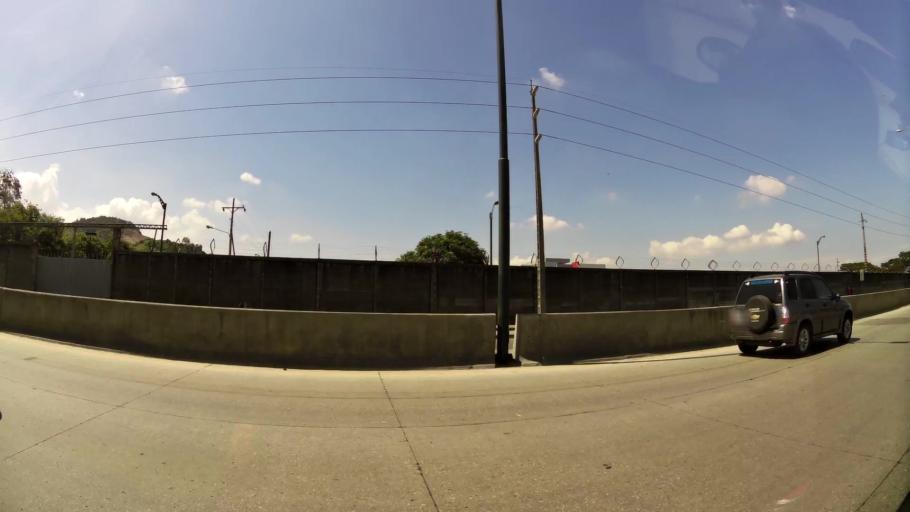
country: EC
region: Guayas
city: Guayaquil
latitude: -2.1932
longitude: -79.9393
